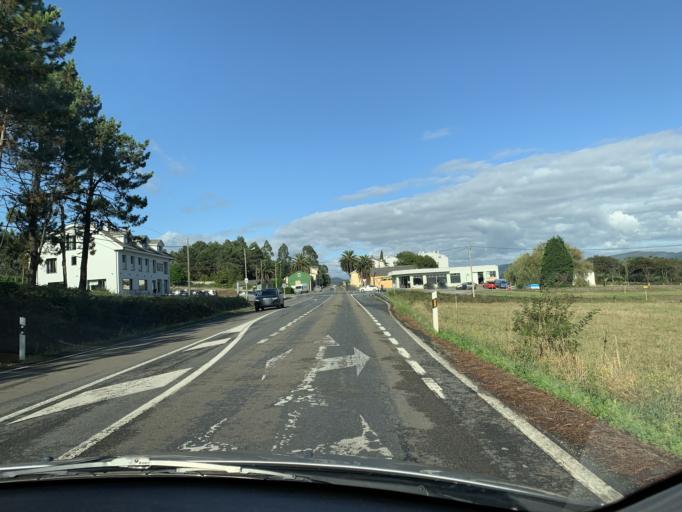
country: ES
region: Galicia
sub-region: Provincia de Lugo
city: Barreiros
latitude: 43.5447
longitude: -7.2163
